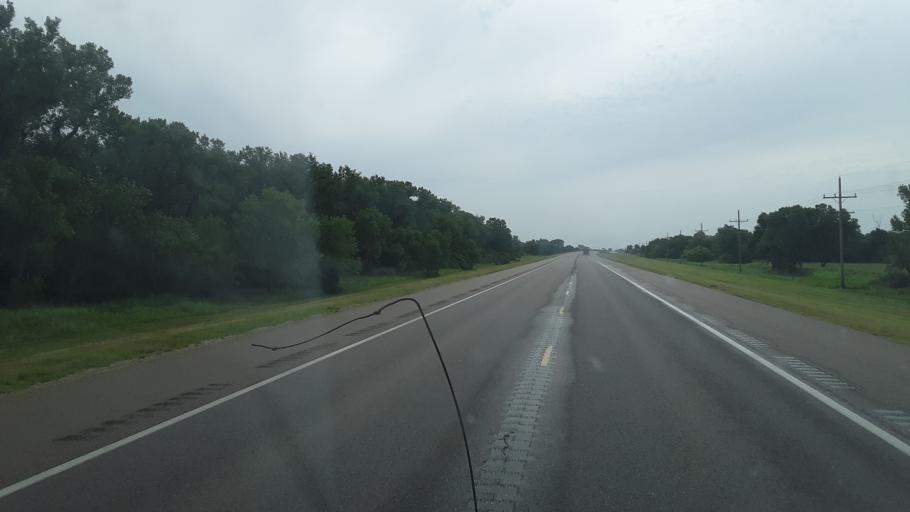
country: US
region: Kansas
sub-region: Edwards County
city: Kinsley
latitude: 37.9280
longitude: -99.3825
